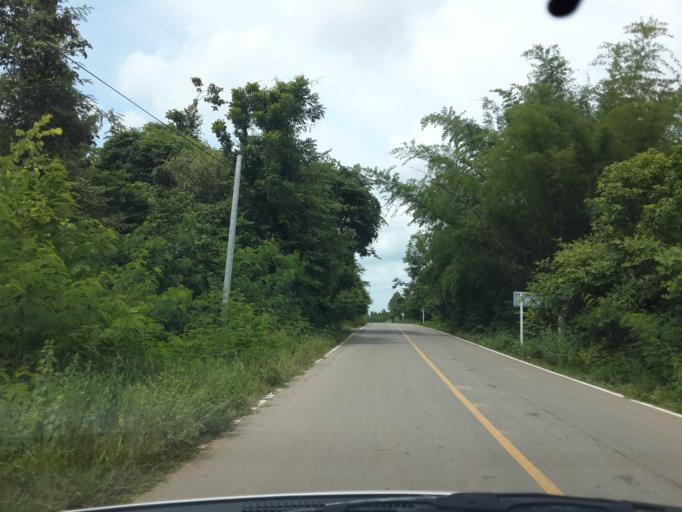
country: TH
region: Ratchaburi
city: Pak Tho
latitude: 13.3703
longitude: 99.6895
